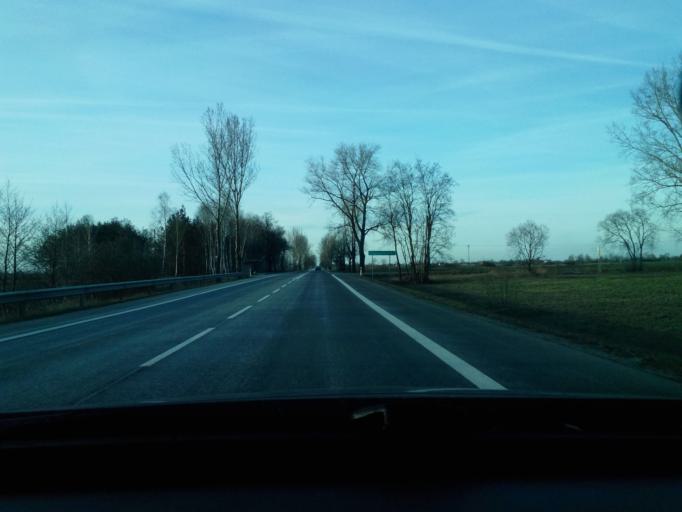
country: PL
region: Kujawsko-Pomorskie
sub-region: Powiat wloclawski
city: Lubien Kujawski
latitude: 52.4252
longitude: 19.1640
